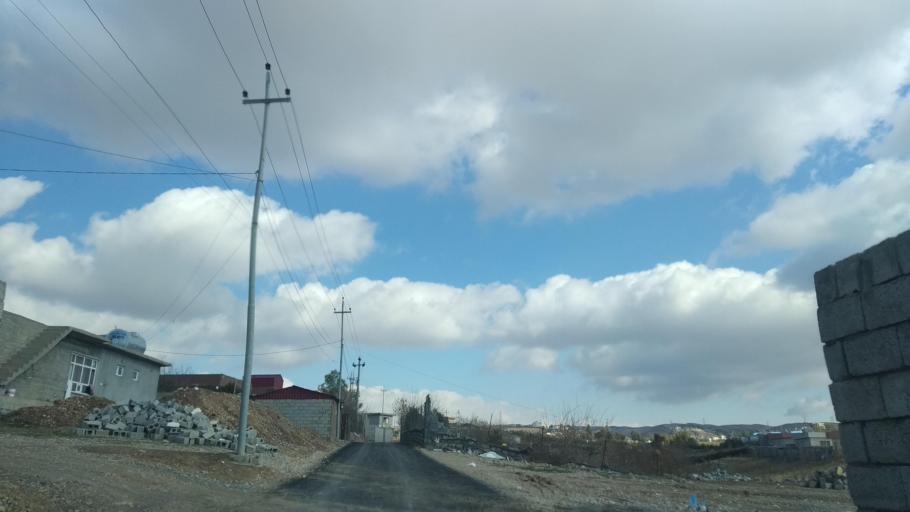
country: IQ
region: Arbil
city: Erbil
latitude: 36.2321
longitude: 44.1537
